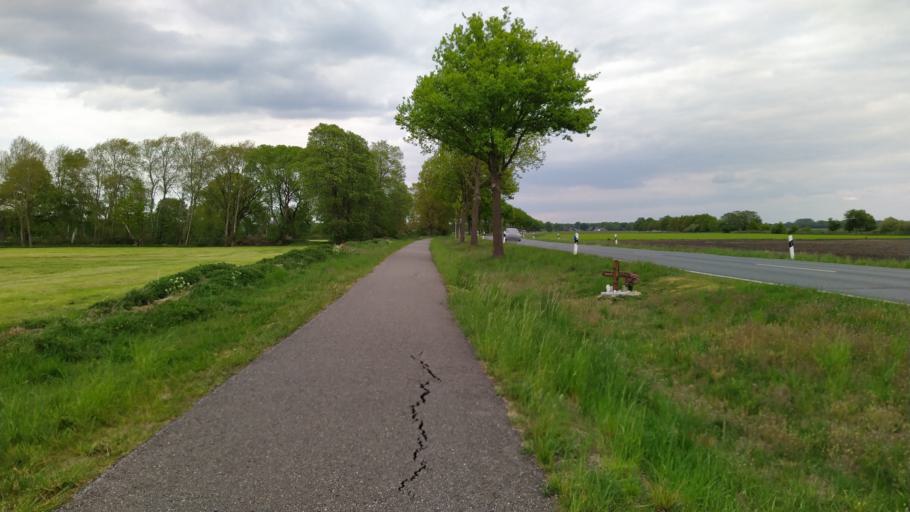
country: DE
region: Lower Saxony
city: Tarmstedt
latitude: 53.2090
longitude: 9.0406
